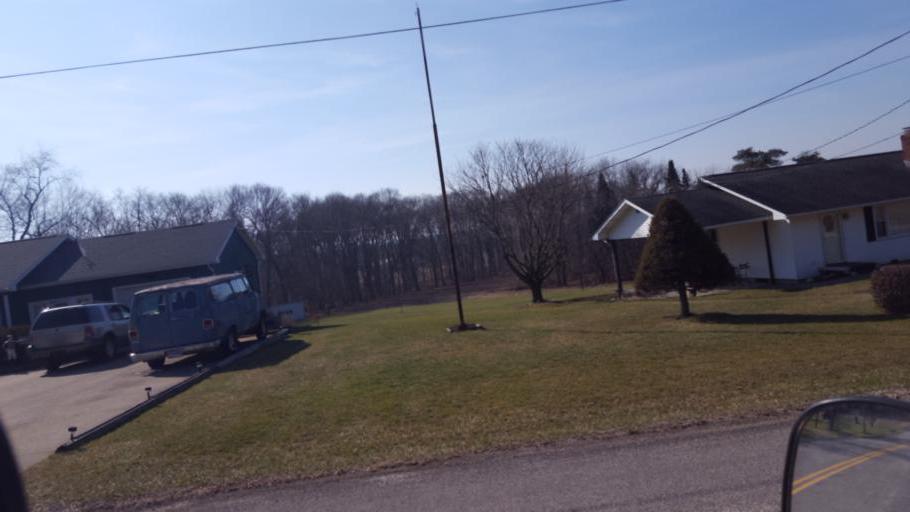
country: US
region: Ohio
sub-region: Ashland County
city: Ashland
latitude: 40.8009
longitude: -82.1871
